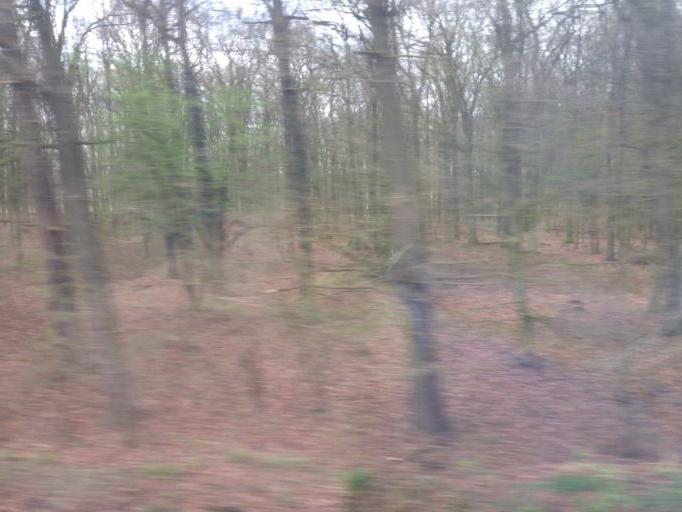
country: DE
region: North Rhine-Westphalia
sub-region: Regierungsbezirk Munster
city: Senden
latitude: 51.9185
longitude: 7.5494
